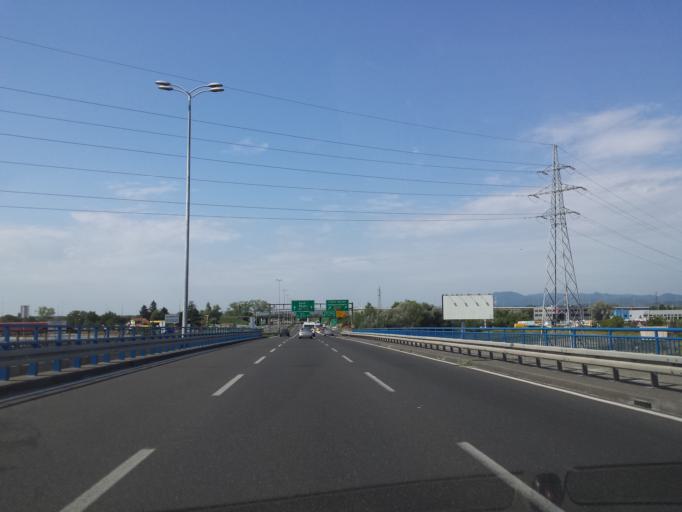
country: HR
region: Grad Zagreb
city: Zadvorsko
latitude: 45.7612
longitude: 15.9059
